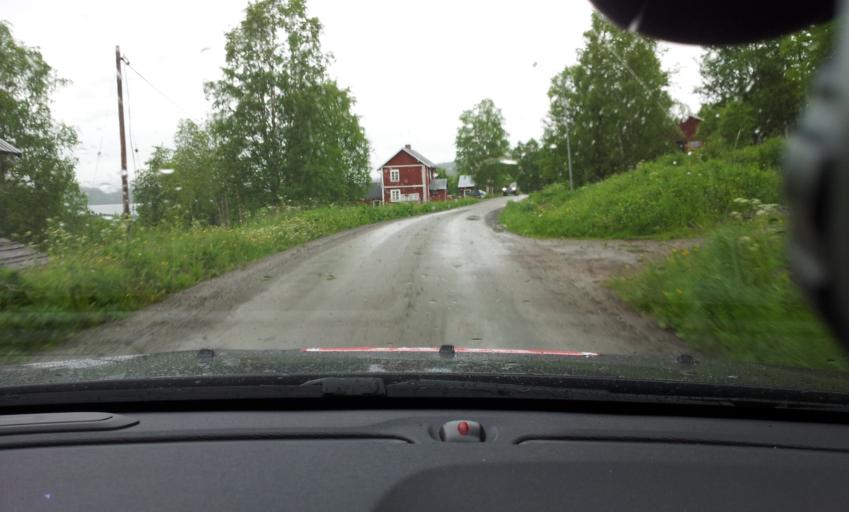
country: SE
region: Jaemtland
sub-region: Are Kommun
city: Are
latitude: 63.4677
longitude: 12.8113
